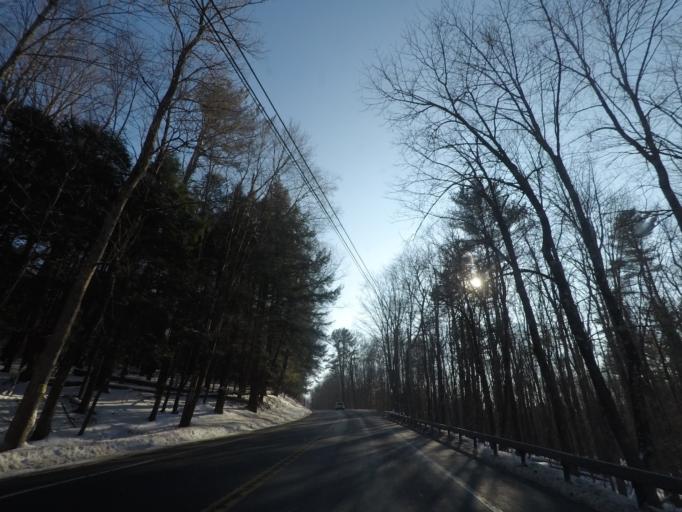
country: US
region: Massachusetts
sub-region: Berkshire County
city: Richmond
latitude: 42.5021
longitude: -73.3687
